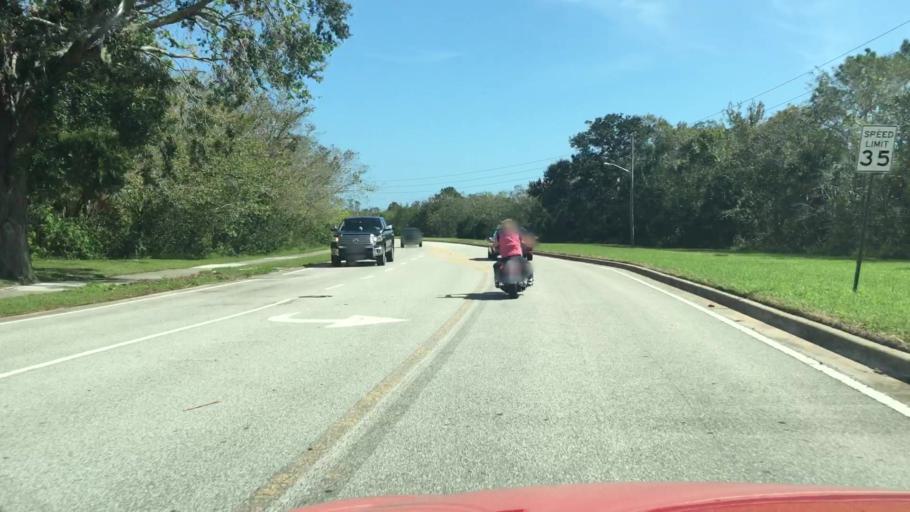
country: US
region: Florida
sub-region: Volusia County
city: South Daytona
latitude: 29.1417
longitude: -81.0425
